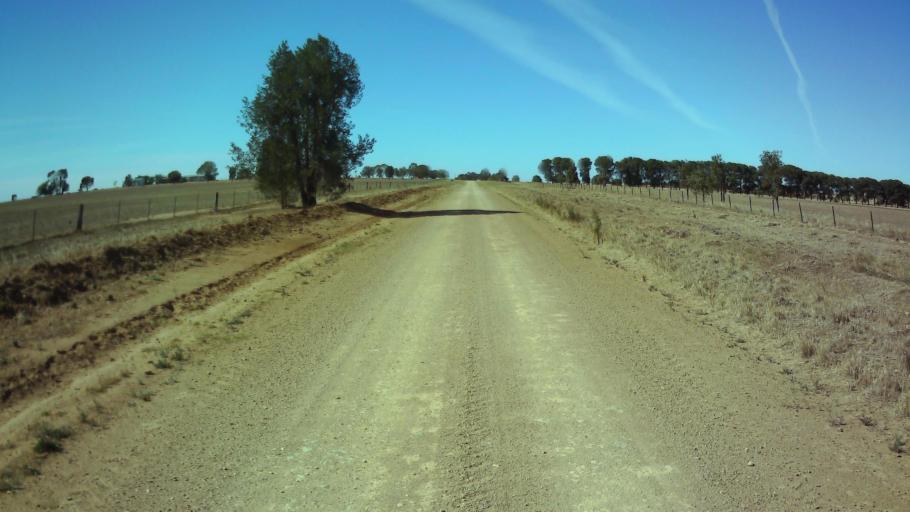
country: AU
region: New South Wales
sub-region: Weddin
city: Grenfell
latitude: -34.0511
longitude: 148.1728
